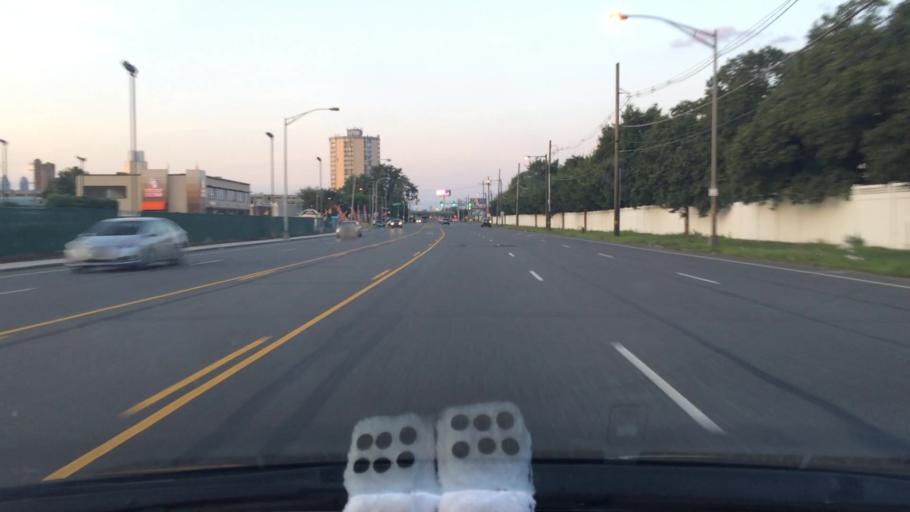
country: US
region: New Jersey
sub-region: Gloucester County
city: National Park
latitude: 39.9090
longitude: -75.1878
